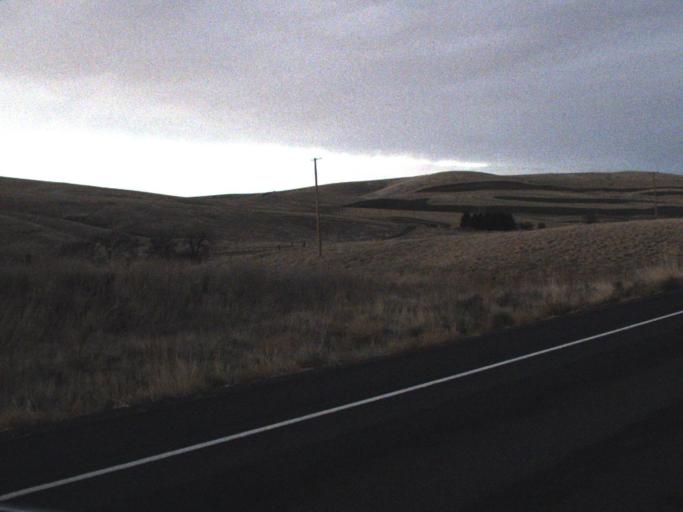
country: US
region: Washington
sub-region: Columbia County
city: Dayton
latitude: 46.5400
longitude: -117.8998
